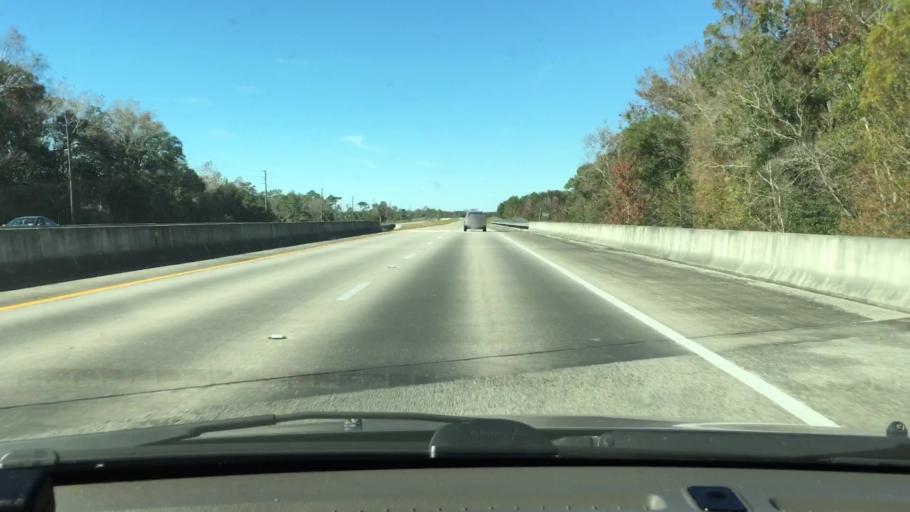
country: US
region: Florida
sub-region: Osceola County
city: Saint Cloud
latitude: 28.1305
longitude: -81.0017
